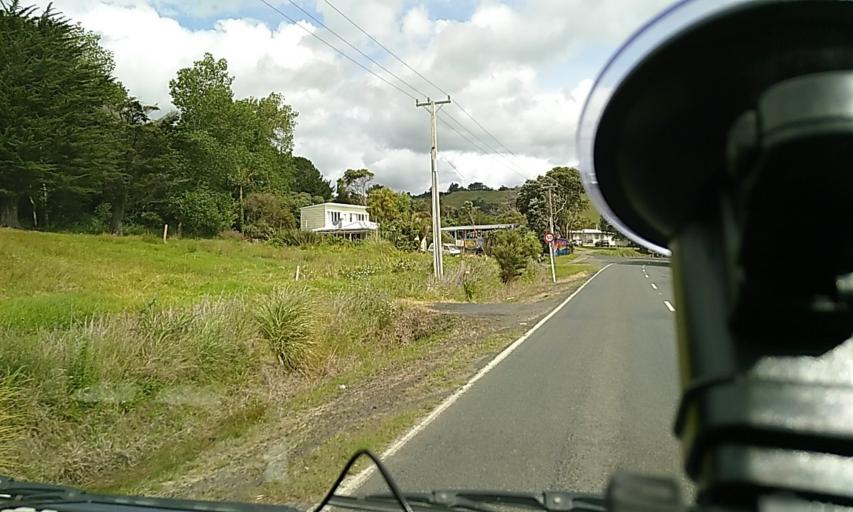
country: NZ
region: Northland
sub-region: Far North District
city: Ahipara
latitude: -35.5241
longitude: 173.3897
